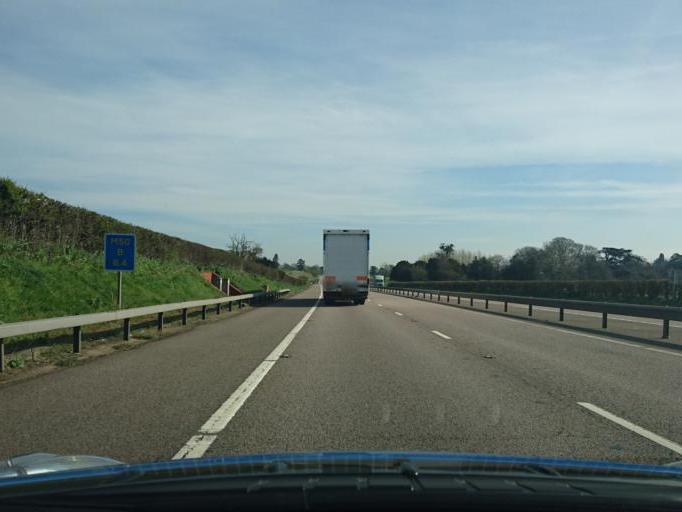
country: GB
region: England
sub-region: Worcestershire
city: Upton upon Severn
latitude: 52.0228
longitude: -2.2117
